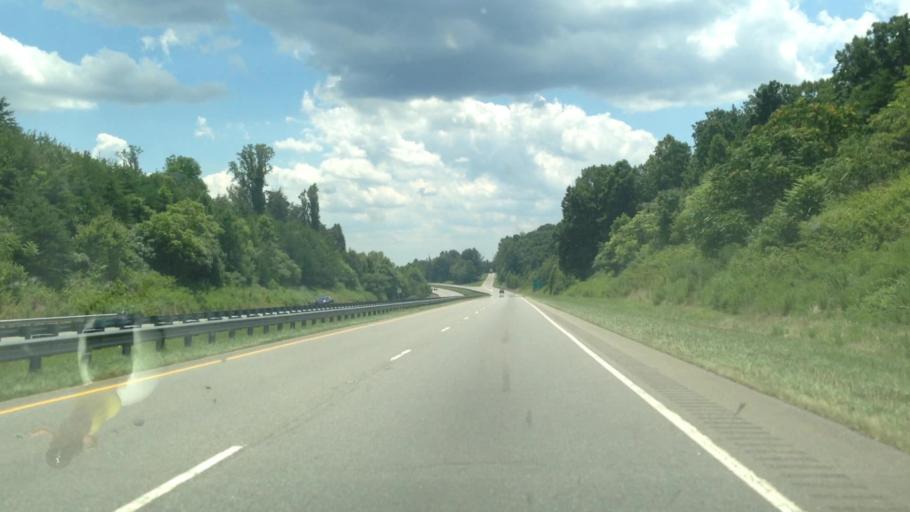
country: US
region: North Carolina
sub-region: Rockingham County
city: Stoneville
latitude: 36.4760
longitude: -79.9251
